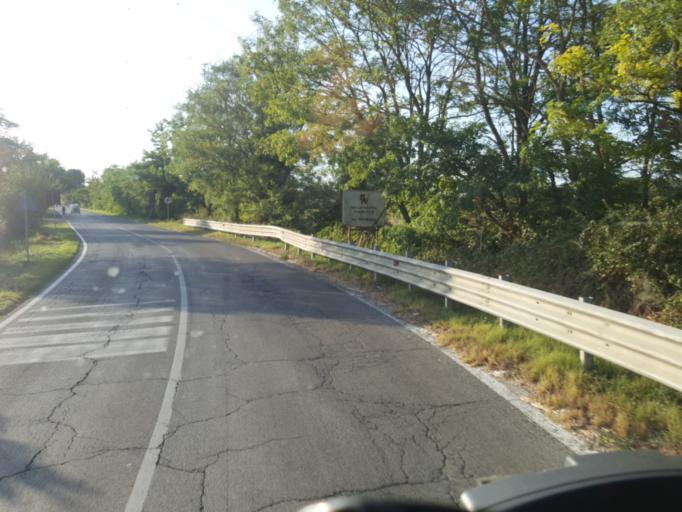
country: IT
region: Latium
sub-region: Citta metropolitana di Roma Capitale
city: Bivio di Capanelle
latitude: 42.1268
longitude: 12.5749
